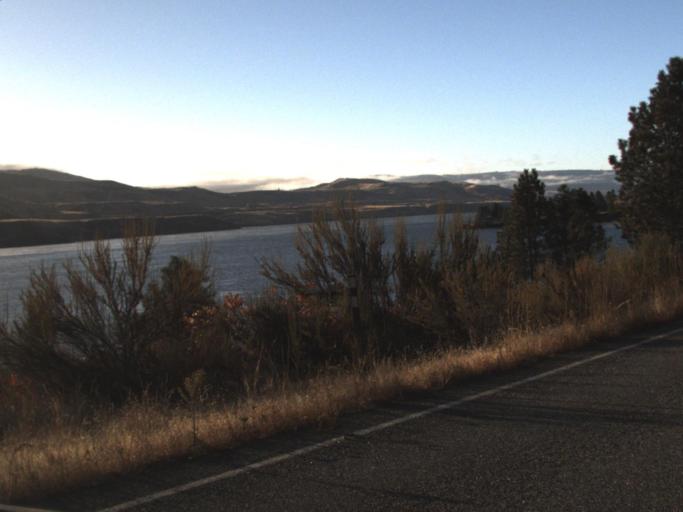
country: US
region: Washington
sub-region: Okanogan County
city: Coulee Dam
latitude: 48.0079
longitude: -118.6864
